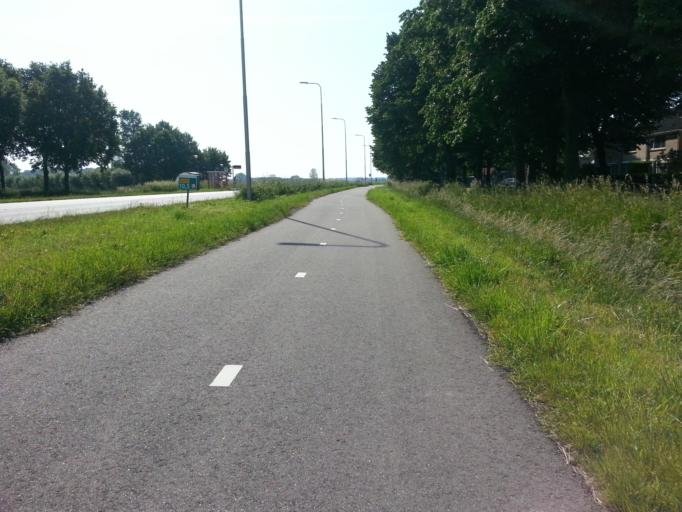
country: NL
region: Utrecht
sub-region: Gemeente Utrechtse Heuvelrug
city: Driebergen-Rijsenburg
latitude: 52.0274
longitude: 5.2482
